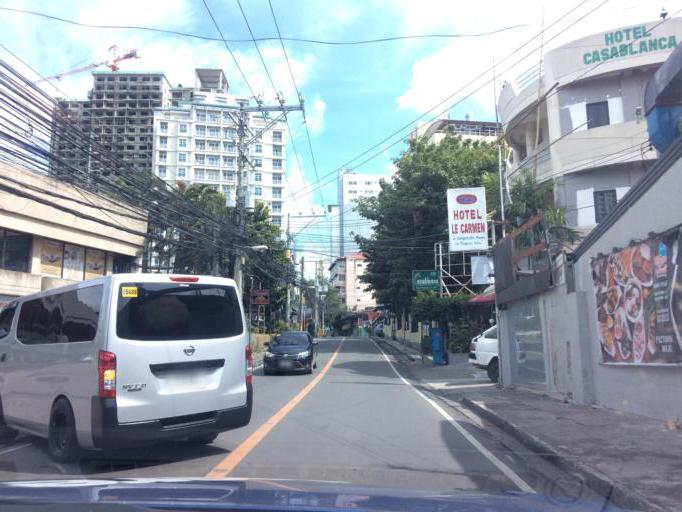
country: PH
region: Central Visayas
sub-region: Province of Cebu
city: Cebu City
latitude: 10.3114
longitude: 123.8952
